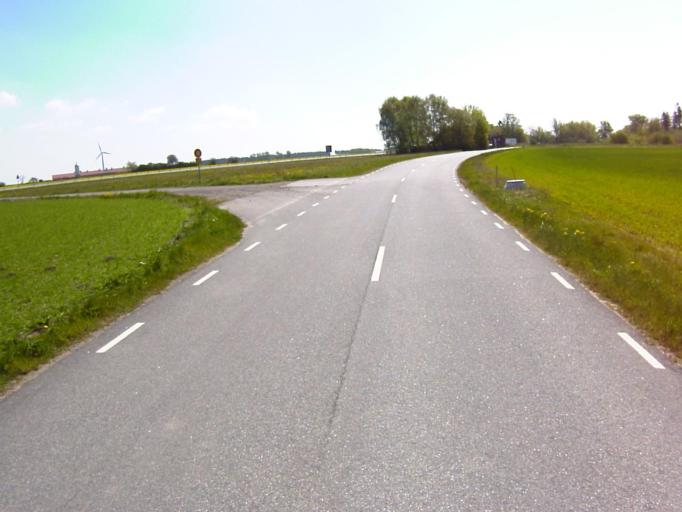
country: SE
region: Skane
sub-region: Kristianstads Kommun
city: Fjalkinge
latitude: 56.0081
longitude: 14.2593
